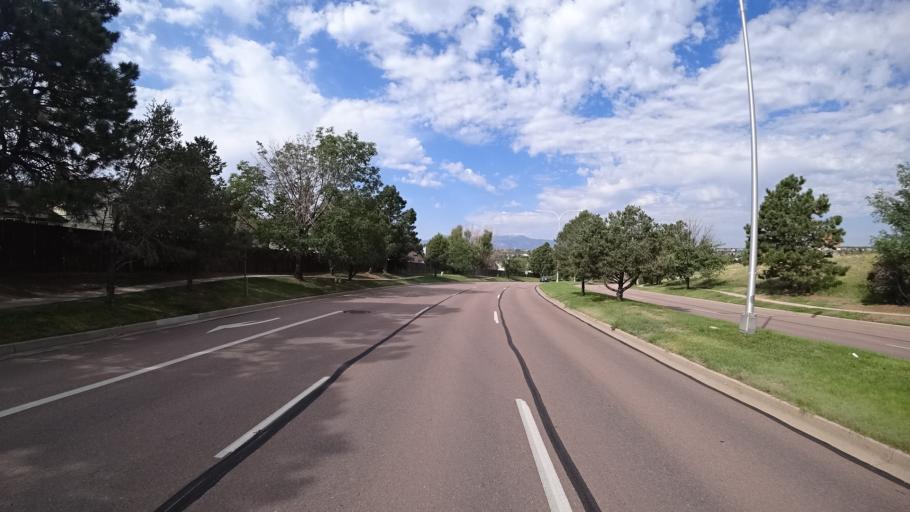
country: US
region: Colorado
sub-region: El Paso County
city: Cimarron Hills
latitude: 38.8989
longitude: -104.7046
